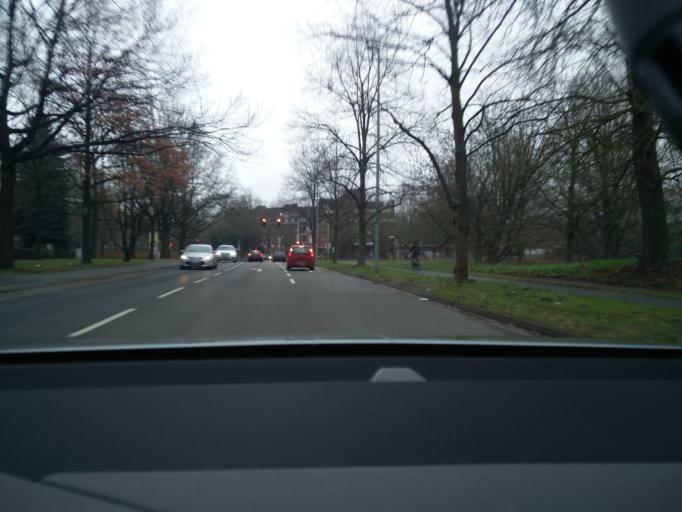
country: DE
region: Lower Saxony
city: Hemmingen
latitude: 52.3359
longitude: 9.7589
